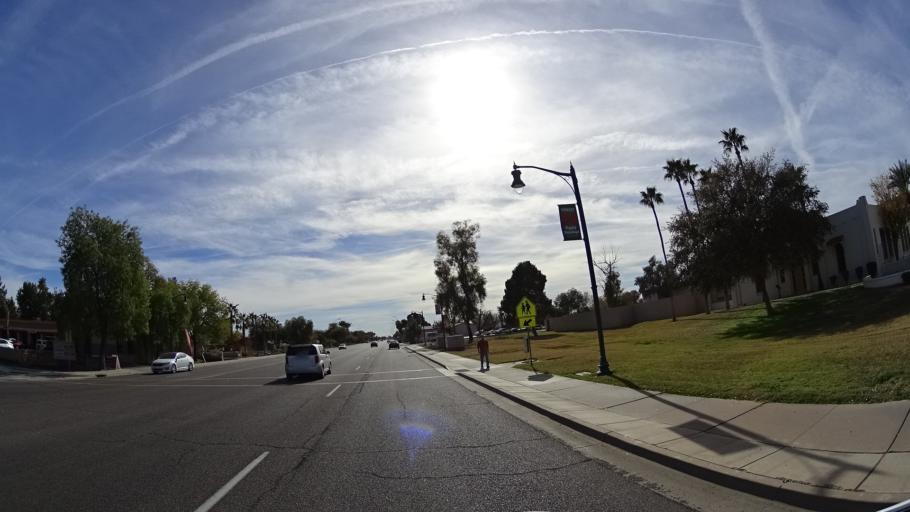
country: US
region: Arizona
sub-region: Maricopa County
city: Gilbert
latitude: 33.3479
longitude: -111.7897
